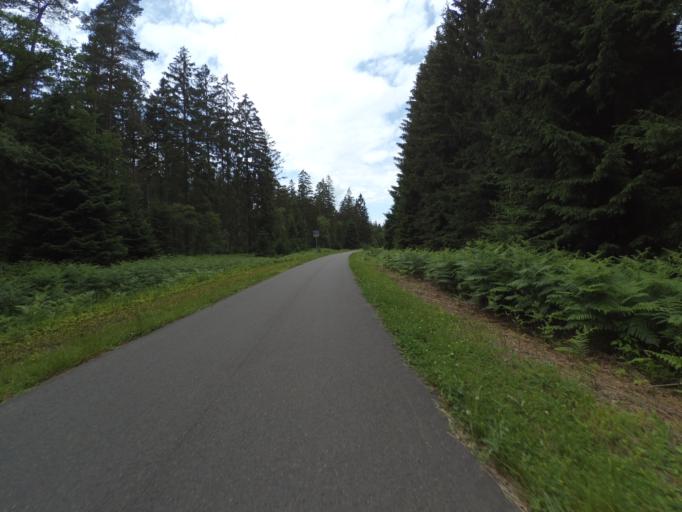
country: DE
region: North Rhine-Westphalia
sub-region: Regierungsbezirk Koln
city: Roetgen
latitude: 50.6450
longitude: 6.2370
